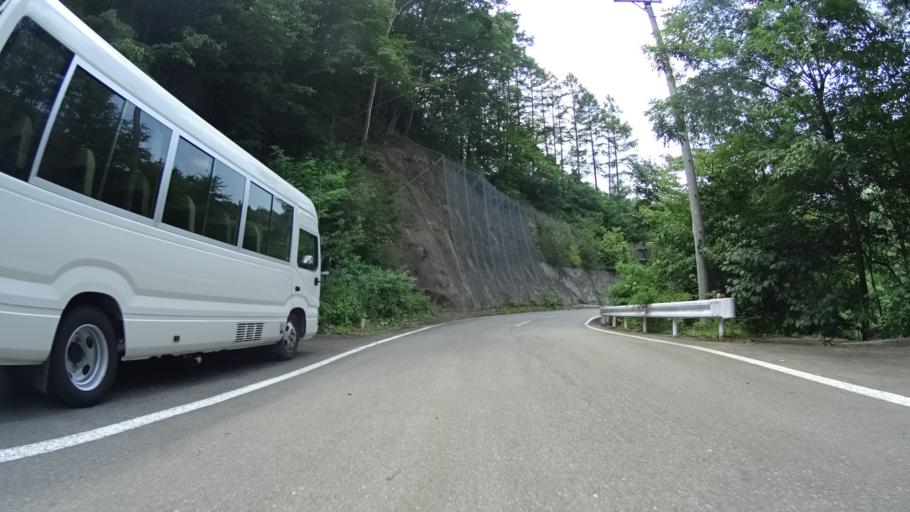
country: JP
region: Nagano
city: Saku
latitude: 36.1164
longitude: 138.6157
